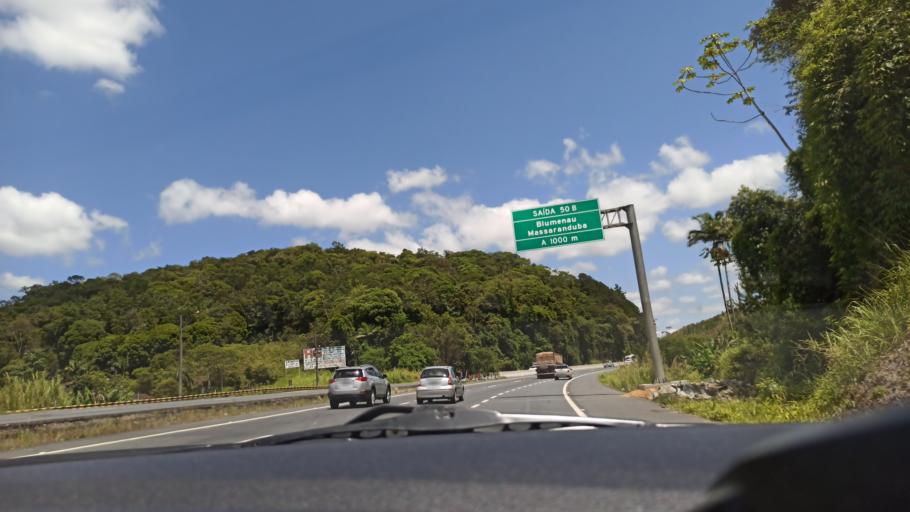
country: BR
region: Santa Catarina
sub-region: Blumenau
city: Blumenau
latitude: -26.8614
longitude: -49.0698
